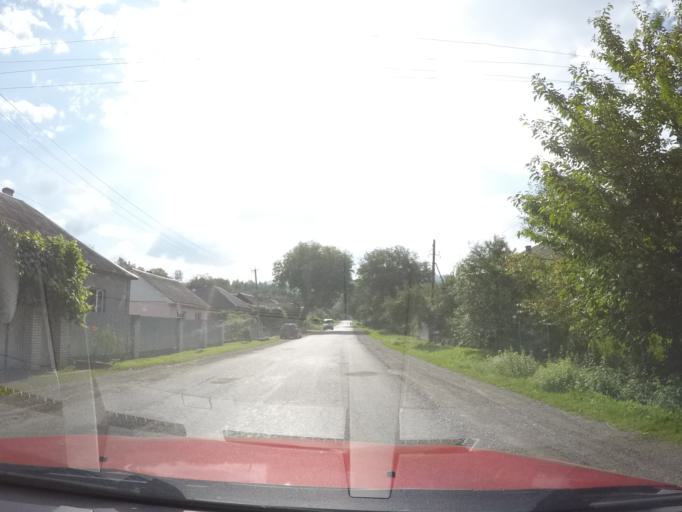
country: UA
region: Zakarpattia
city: Velykyi Bereznyi
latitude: 48.9419
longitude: 22.5850
